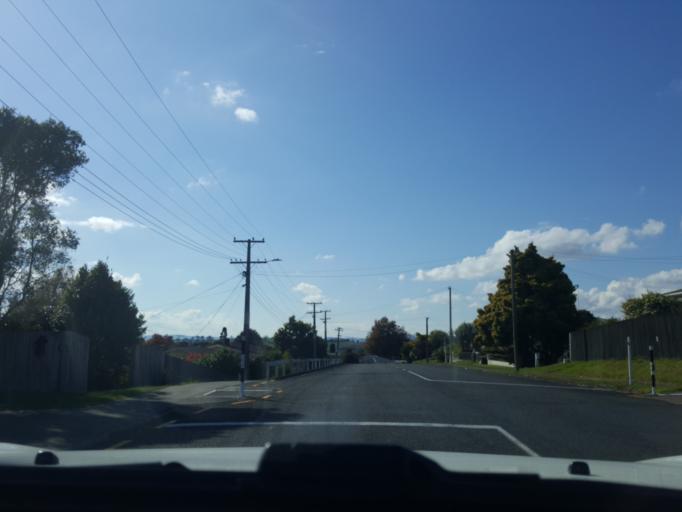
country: NZ
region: Waikato
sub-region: Waikato District
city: Ngaruawahia
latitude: -37.5433
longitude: 175.1699
